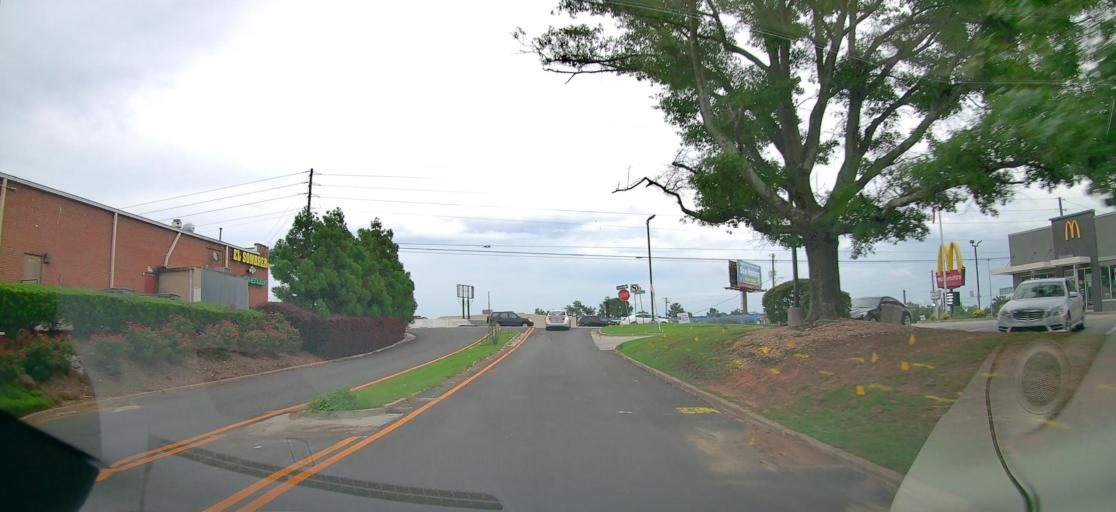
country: US
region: Georgia
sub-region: Bibb County
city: Macon
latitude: 32.8495
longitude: -83.6260
